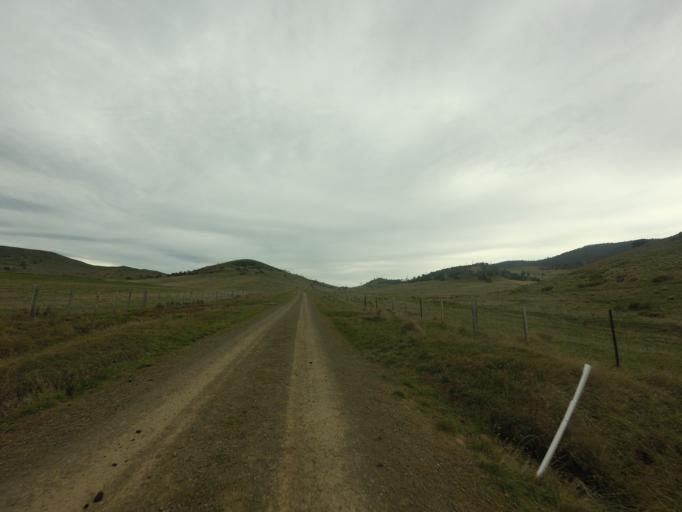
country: AU
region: Tasmania
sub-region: Derwent Valley
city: New Norfolk
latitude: -42.3847
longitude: 146.8726
